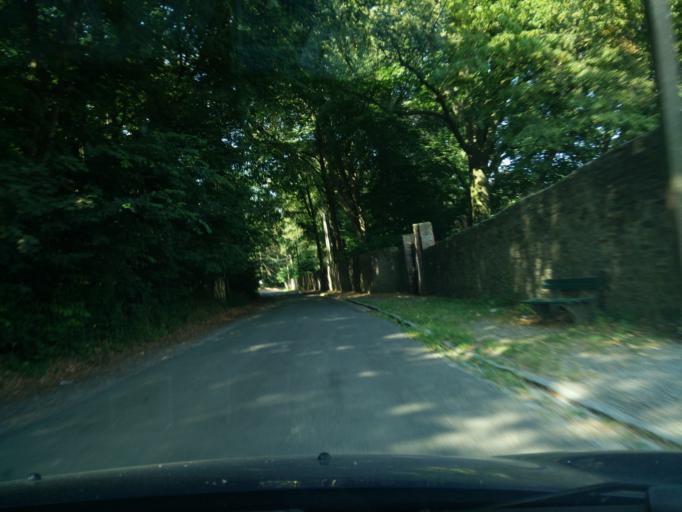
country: BE
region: Wallonia
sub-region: Province du Hainaut
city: Ecaussinnes-d'Enghien
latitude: 50.5746
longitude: 4.1787
